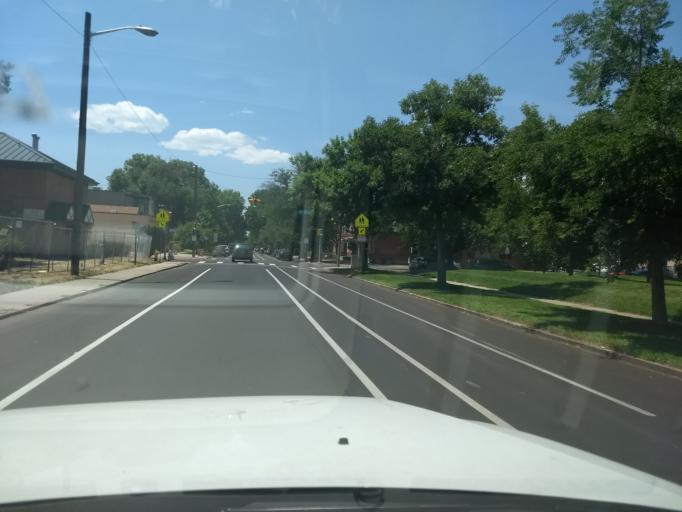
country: US
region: Colorado
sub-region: Denver County
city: Denver
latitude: 39.7599
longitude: -104.9766
